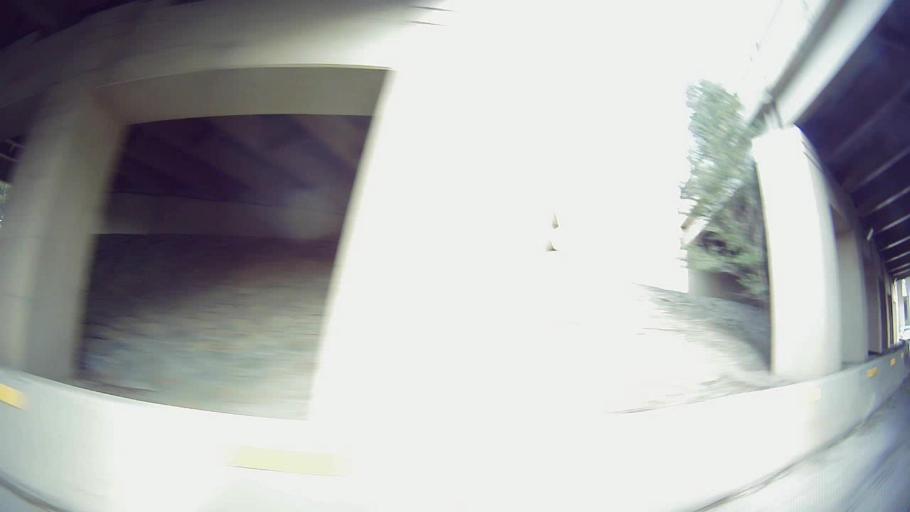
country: US
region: Michigan
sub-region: Wayne County
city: Highland Park
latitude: 42.3982
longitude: -83.1103
